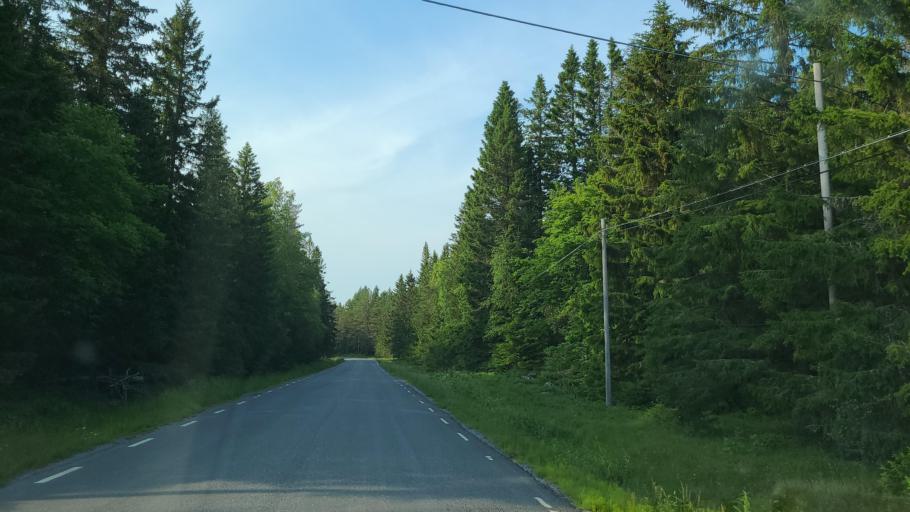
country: SE
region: Vaesterbotten
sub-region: Skelleftea Kommun
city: Skelleftehamn
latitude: 64.4661
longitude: 21.5866
